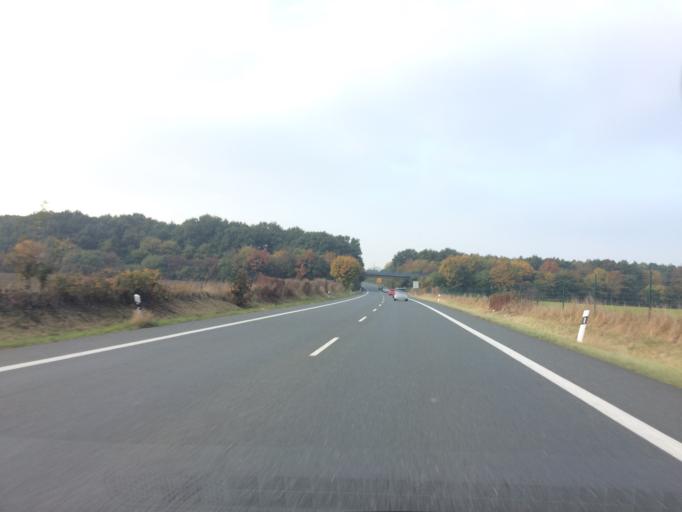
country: DE
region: North Rhine-Westphalia
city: Dorsten
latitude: 51.6798
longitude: 7.0256
